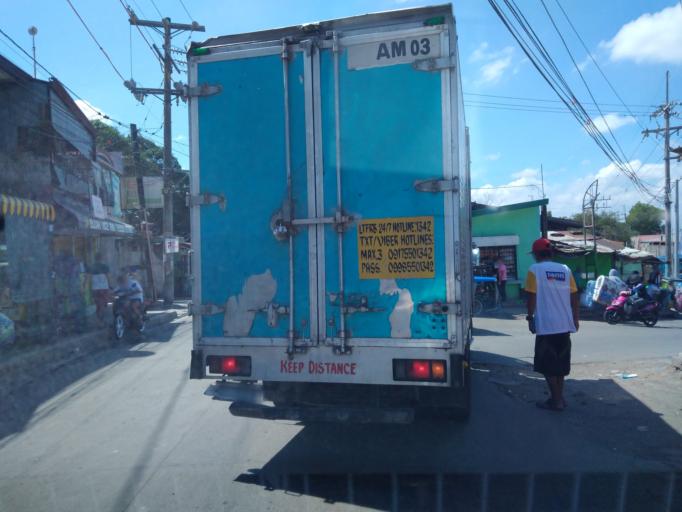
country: PH
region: Central Luzon
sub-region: Province of Bulacan
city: Bitungol
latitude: 14.8586
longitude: 121.0486
